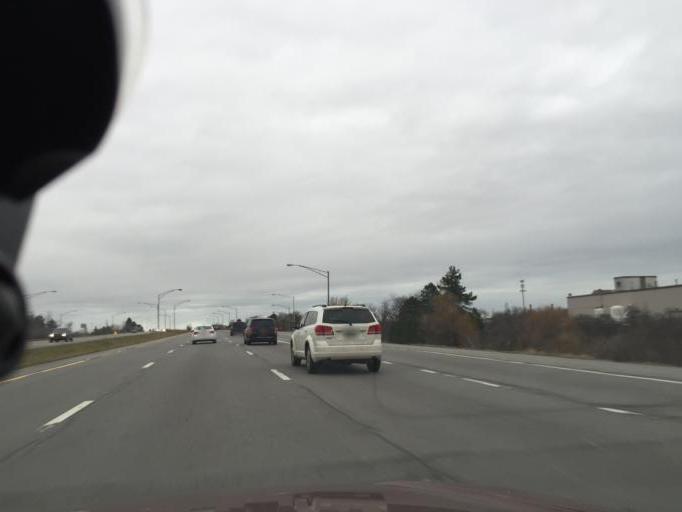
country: US
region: New York
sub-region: Monroe County
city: North Gates
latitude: 43.1755
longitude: -77.6832
